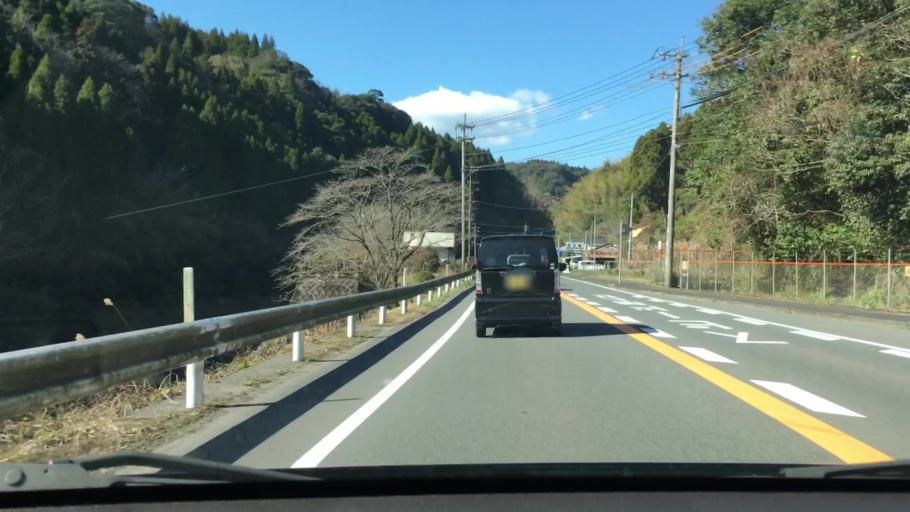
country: JP
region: Kagoshima
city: Kagoshima-shi
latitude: 31.6515
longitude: 130.5020
